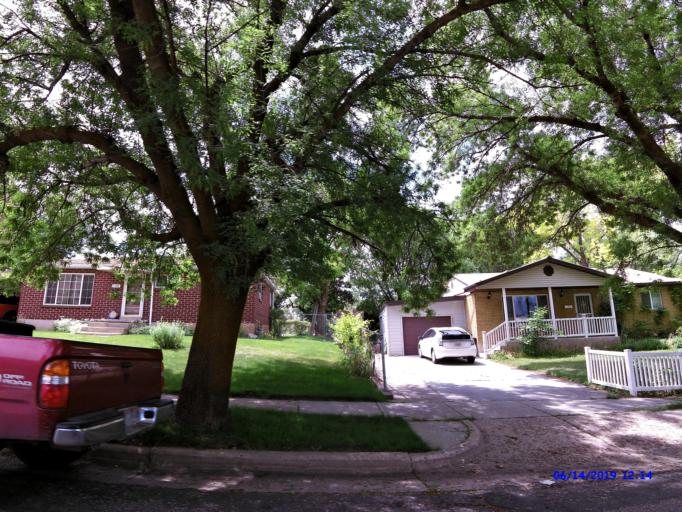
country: US
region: Utah
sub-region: Weber County
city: Ogden
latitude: 41.2568
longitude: -111.9497
